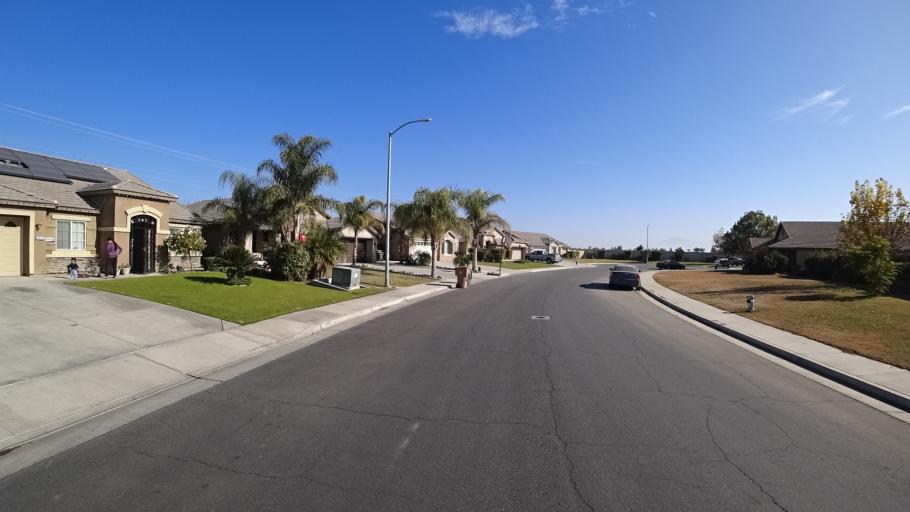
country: US
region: California
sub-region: Kern County
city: Greenfield
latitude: 35.2737
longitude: -119.0580
